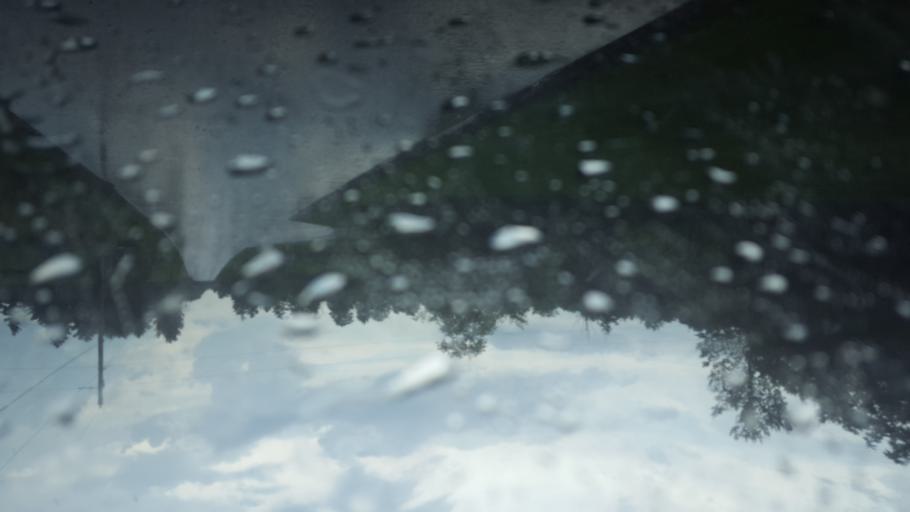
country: US
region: Ohio
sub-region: Richland County
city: Lexington
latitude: 40.6161
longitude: -82.6494
